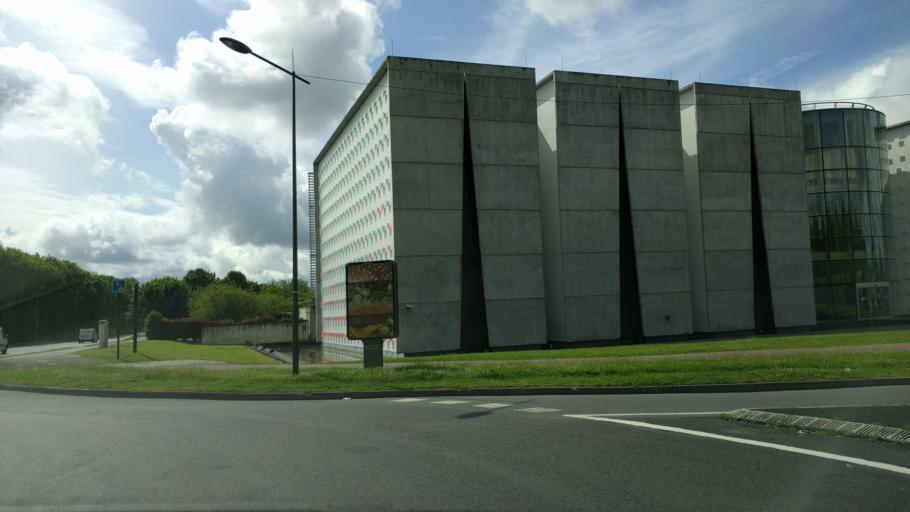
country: FR
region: Ile-de-France
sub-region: Departement de Seine-et-Marne
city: Savigny-le-Temple
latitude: 48.5965
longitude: 2.5877
